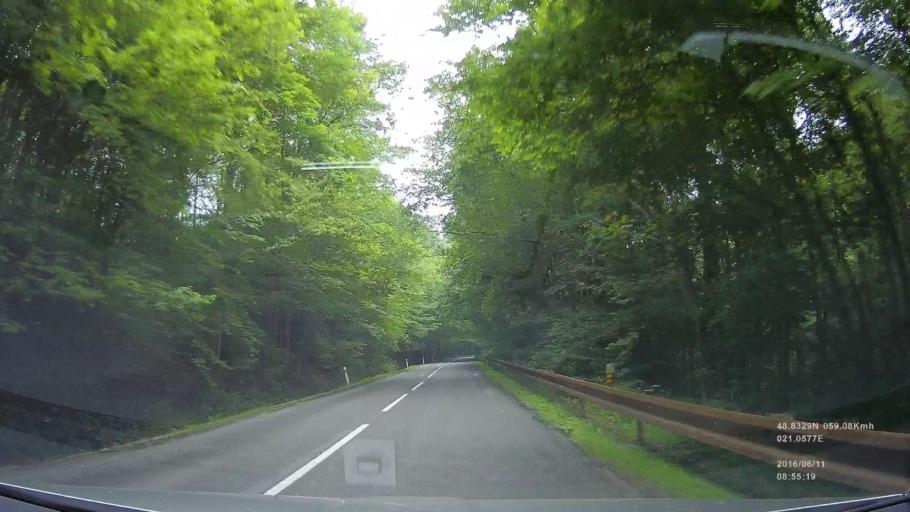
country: SK
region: Kosicky
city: Gelnica
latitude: 48.8124
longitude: 21.0942
